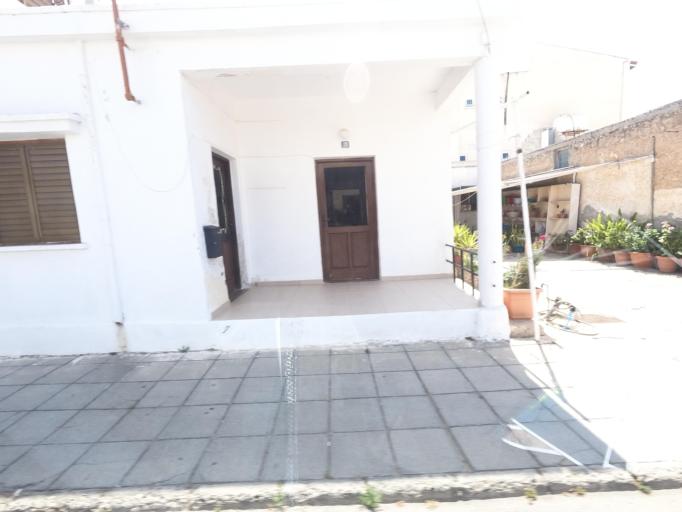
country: CY
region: Ammochostos
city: Paralimni
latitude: 35.0412
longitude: 33.9813
